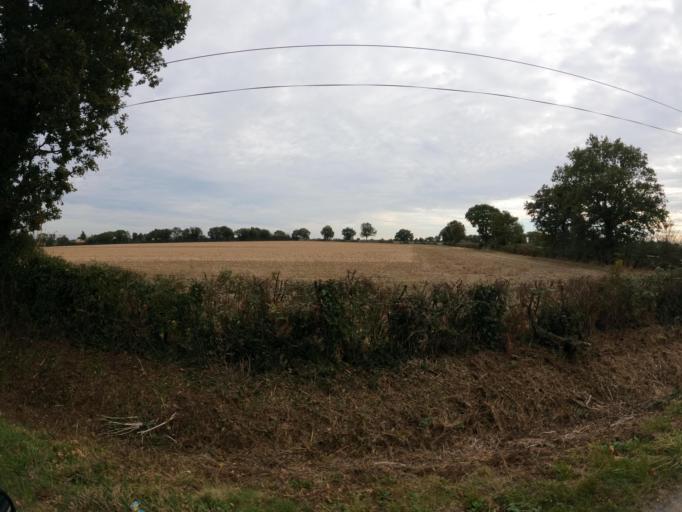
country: FR
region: Pays de la Loire
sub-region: Departement de Maine-et-Loire
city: Saint-Christophe-du-Bois
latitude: 47.0187
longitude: -0.9919
